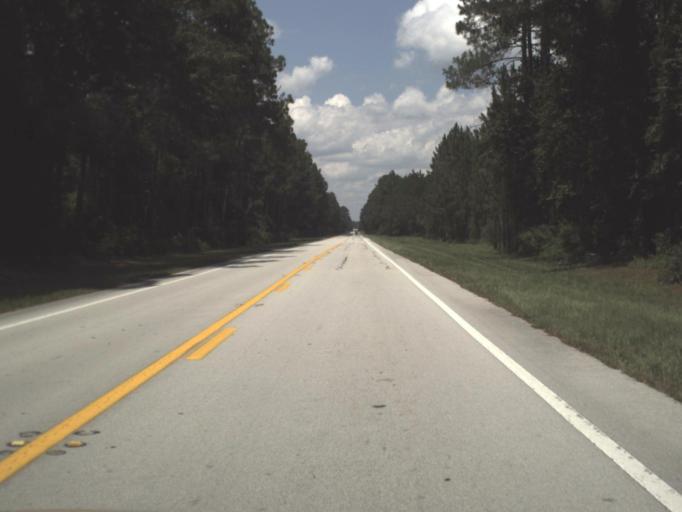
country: US
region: Florida
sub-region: Baker County
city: Macclenny
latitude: 30.1456
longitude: -82.1859
